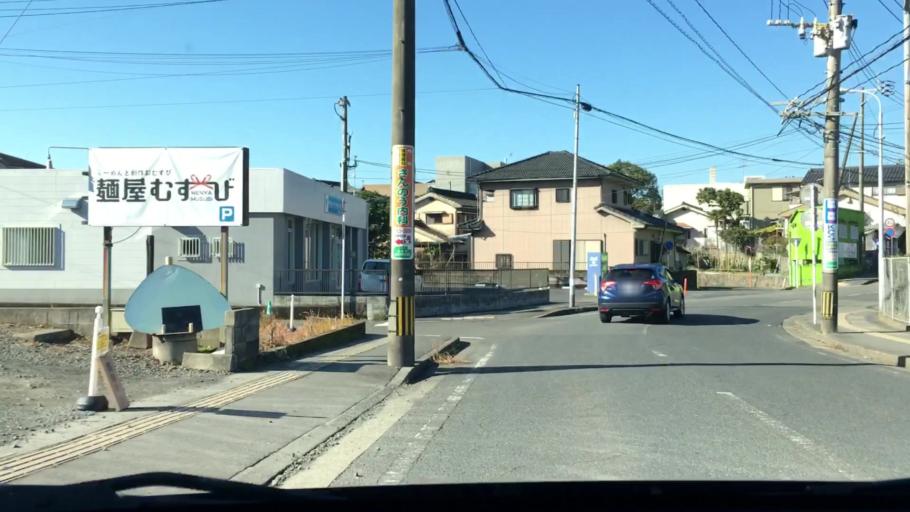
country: JP
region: Kagoshima
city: Kajiki
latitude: 31.7408
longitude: 130.6671
